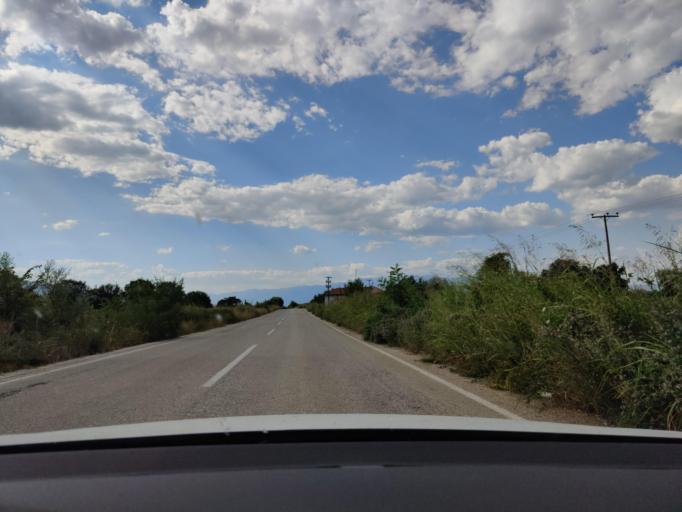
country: GR
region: Central Macedonia
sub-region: Nomos Serron
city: Strymoniko
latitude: 41.0765
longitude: 23.2958
